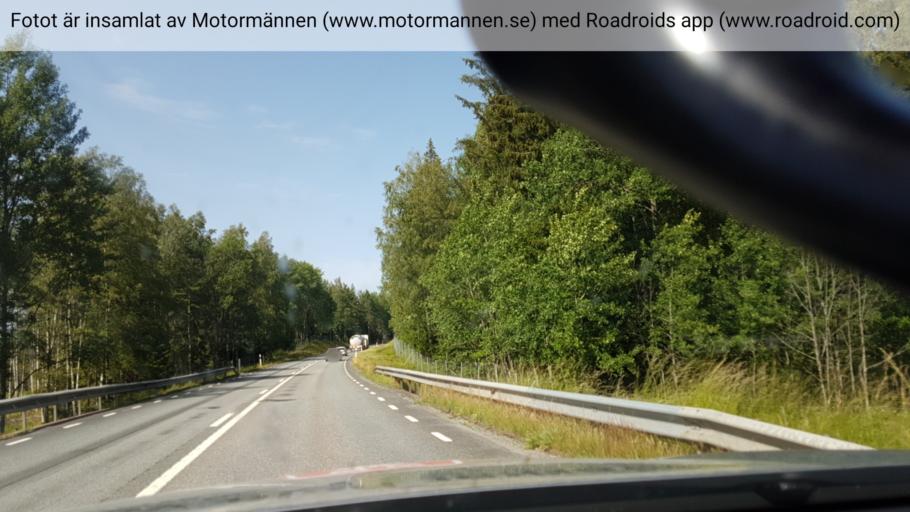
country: SE
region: Joenkoeping
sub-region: Eksjo Kommun
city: Eksjoe
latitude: 57.7231
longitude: 14.9378
